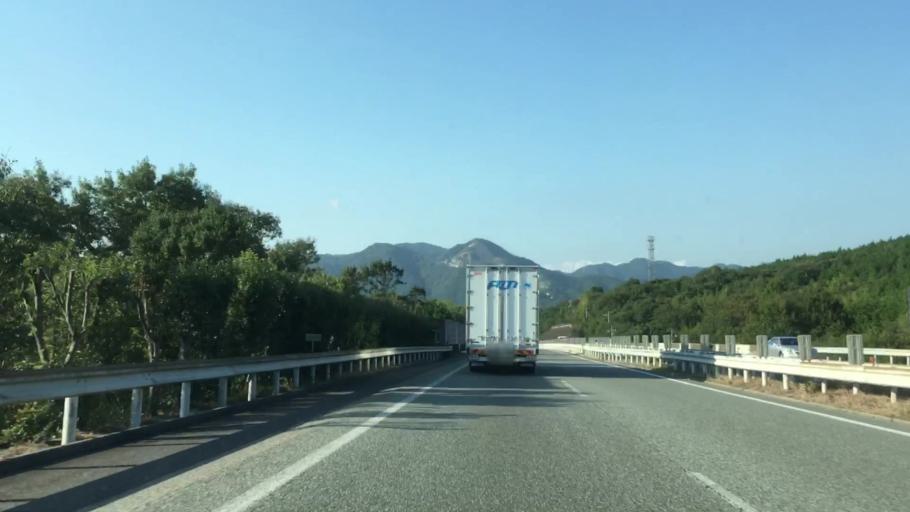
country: JP
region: Yamaguchi
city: Hofu
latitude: 34.0610
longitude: 131.5025
